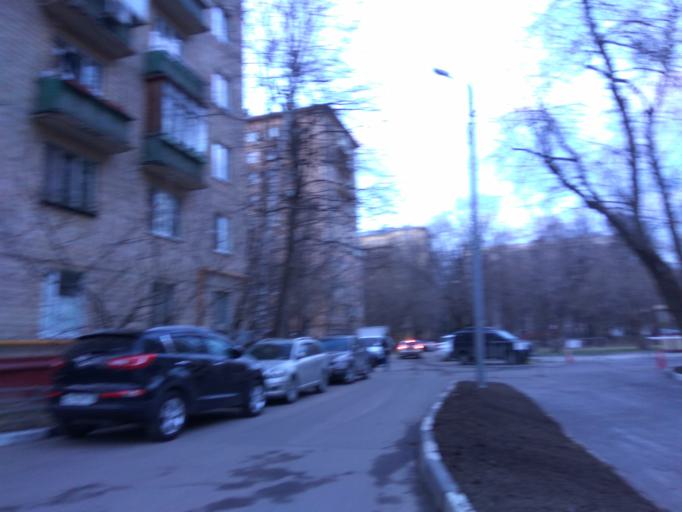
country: RU
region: Moskovskaya
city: Semenovskoye
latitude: 55.6902
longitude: 37.5520
